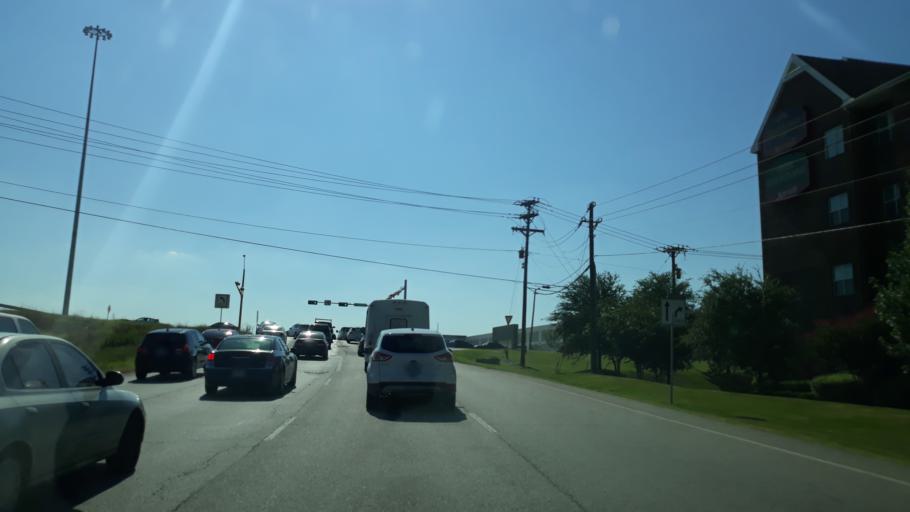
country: US
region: Texas
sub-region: Tarrant County
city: Euless
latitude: 32.8379
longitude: -97.0211
